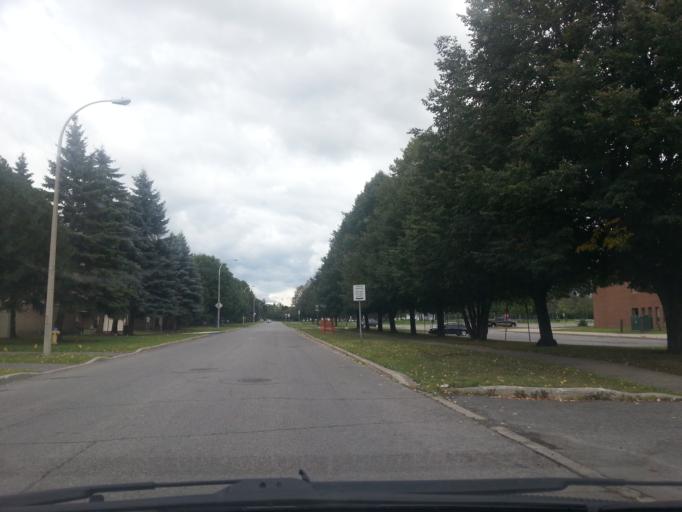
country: CA
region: Quebec
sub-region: Outaouais
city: Gatineau
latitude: 45.4809
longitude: -75.5319
